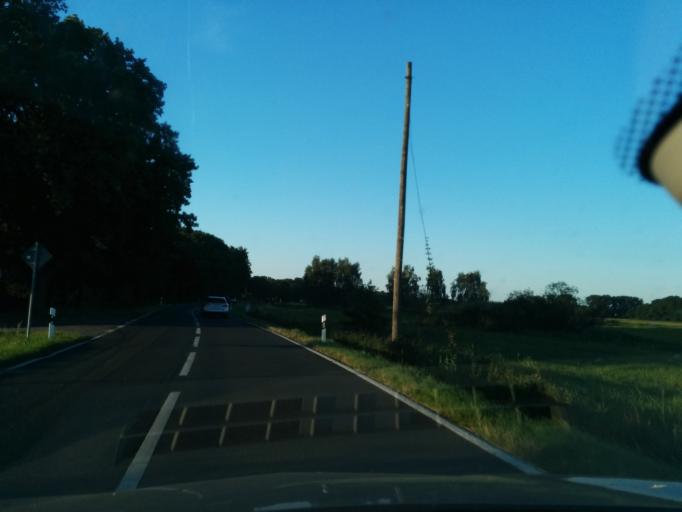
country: DE
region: Mecklenburg-Vorpommern
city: Seebad Bansin
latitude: 53.9764
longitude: 14.0743
